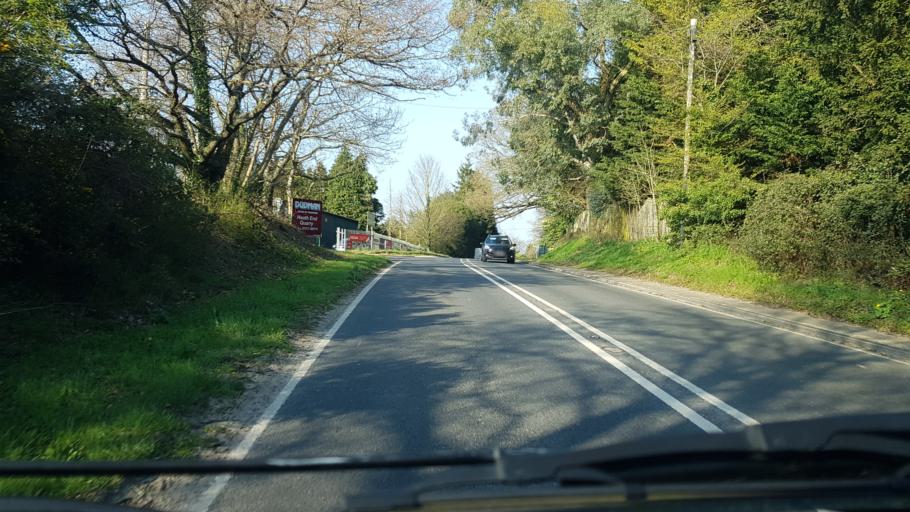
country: GB
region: England
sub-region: West Sussex
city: Petworth
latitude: 50.9596
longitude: -0.6259
